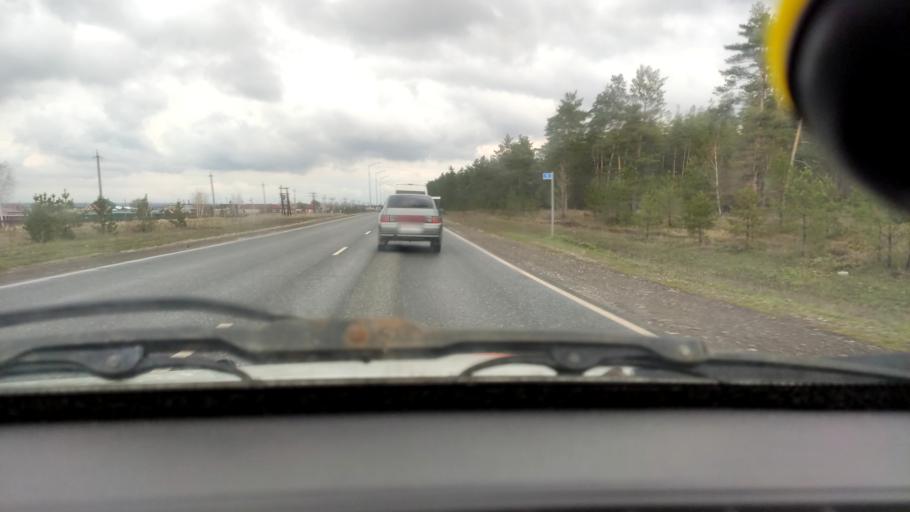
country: RU
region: Samara
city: Zhigulevsk
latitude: 53.5773
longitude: 49.5601
